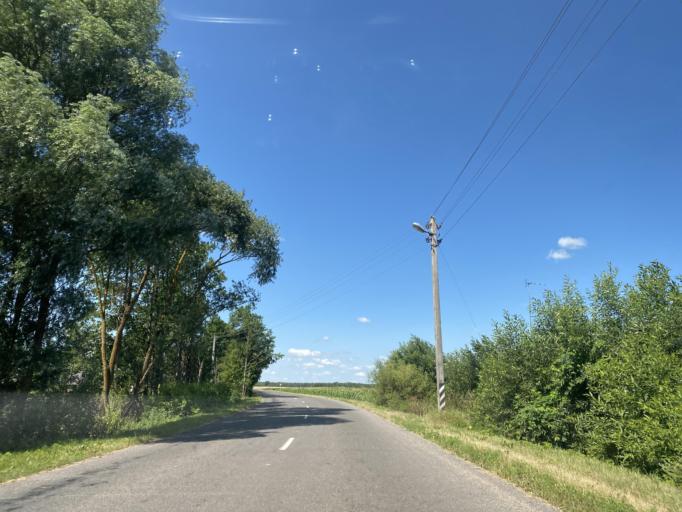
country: BY
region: Brest
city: Ivanava
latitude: 52.2074
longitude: 25.6256
